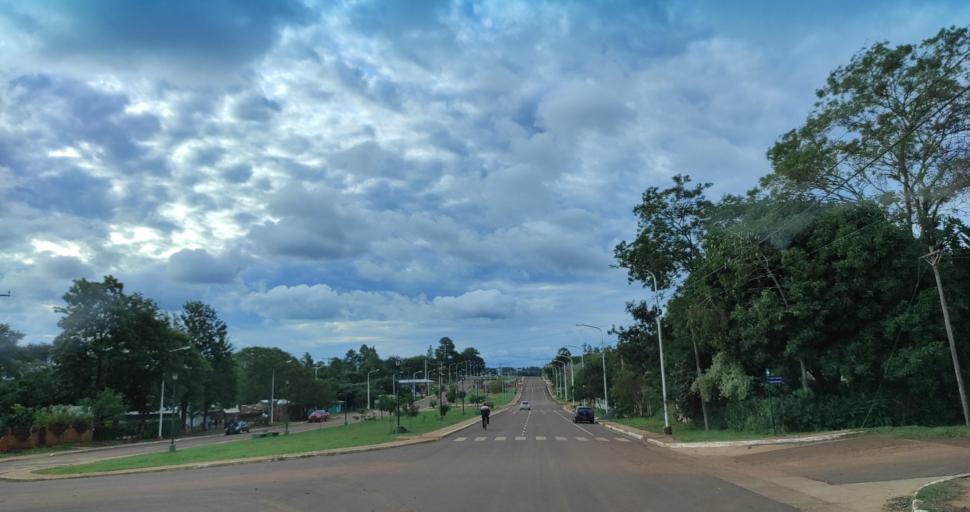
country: AR
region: Misiones
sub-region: Departamento de Candelaria
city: Candelaria
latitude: -27.4554
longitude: -55.7439
